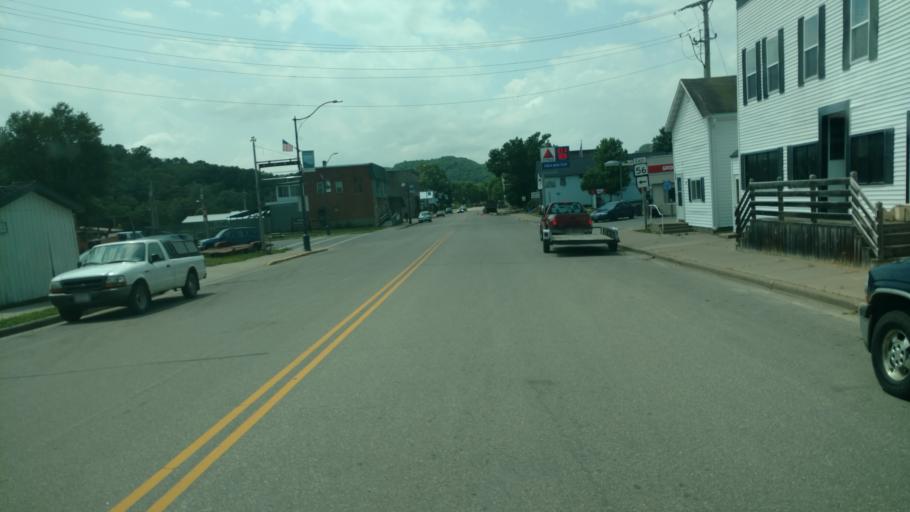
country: US
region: Wisconsin
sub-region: Vernon County
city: Viroqua
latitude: 43.5061
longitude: -90.6675
